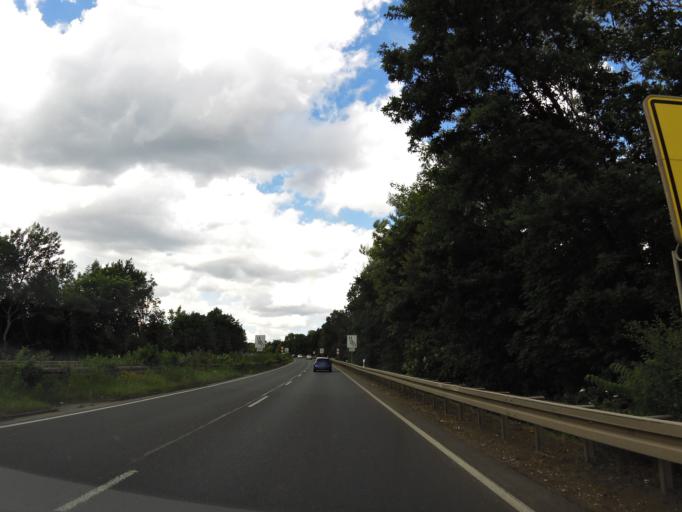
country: DE
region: Saxony
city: Markkleeberg
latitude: 51.2795
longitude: 12.3836
